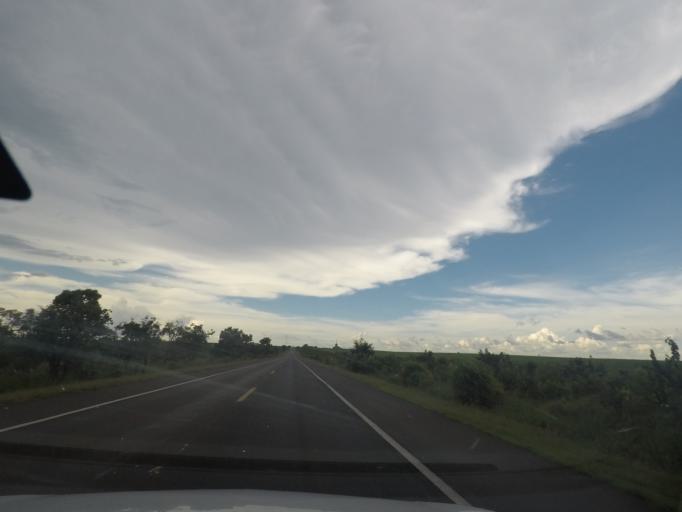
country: BR
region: Minas Gerais
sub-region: Prata
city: Prata
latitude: -19.6117
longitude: -48.8393
